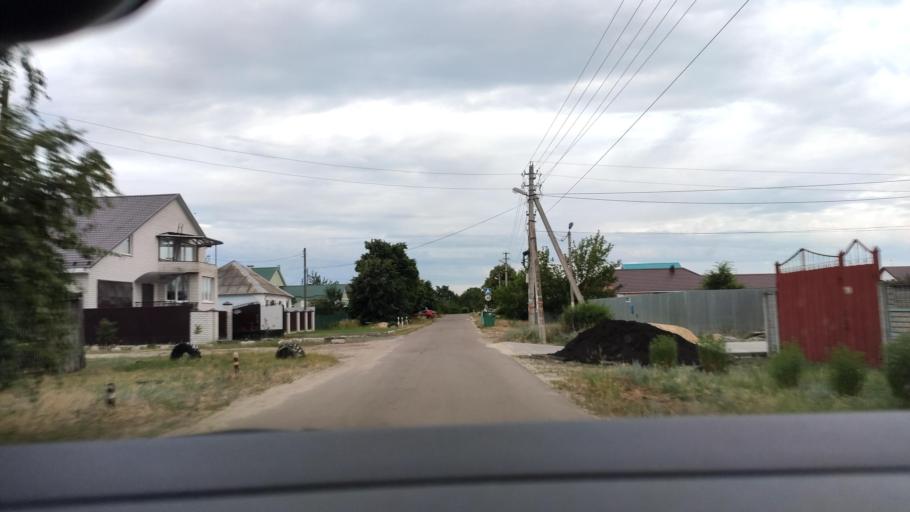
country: RU
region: Voronezj
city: Maslovka
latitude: 51.5667
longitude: 39.2498
